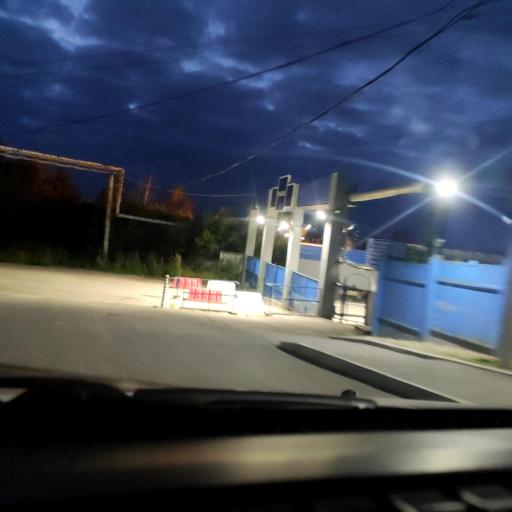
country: RU
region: Perm
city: Polazna
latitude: 58.1535
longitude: 56.4463
